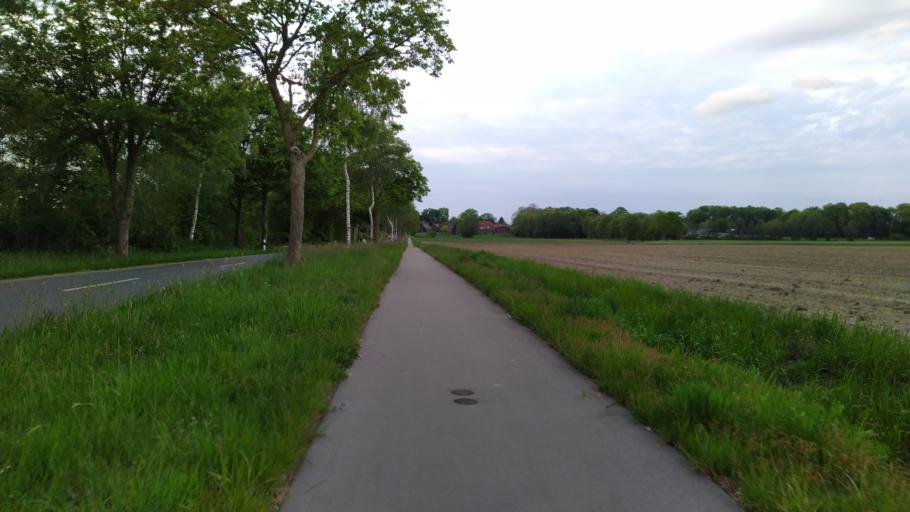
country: DE
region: Lower Saxony
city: Ahlerstedt
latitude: 53.3981
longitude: 9.4047
